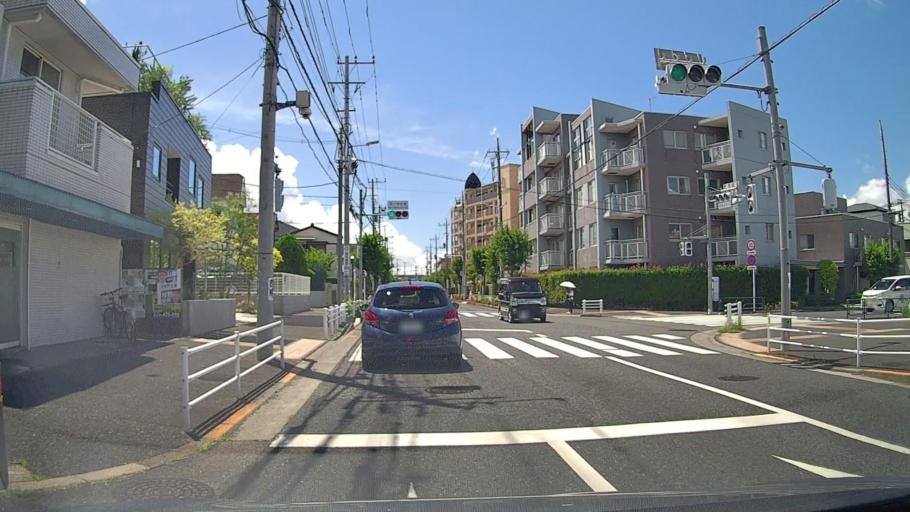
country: JP
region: Tokyo
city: Nishi-Tokyo-shi
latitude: 35.7433
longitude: 139.5657
